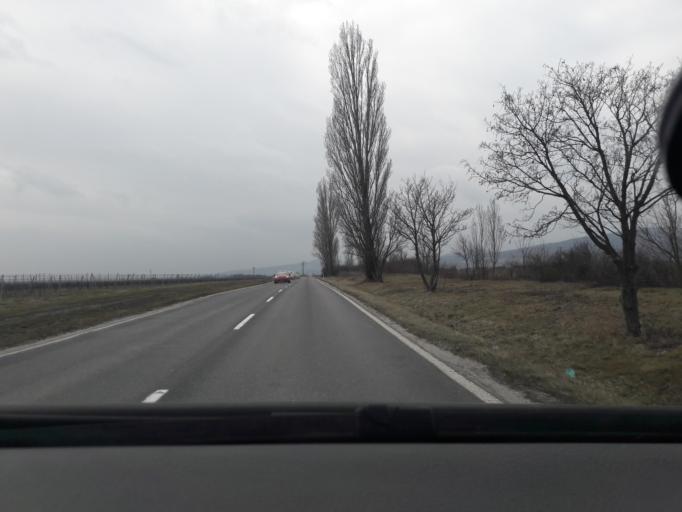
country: SK
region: Trnavsky
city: Smolenice
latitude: 48.4257
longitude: 17.4139
